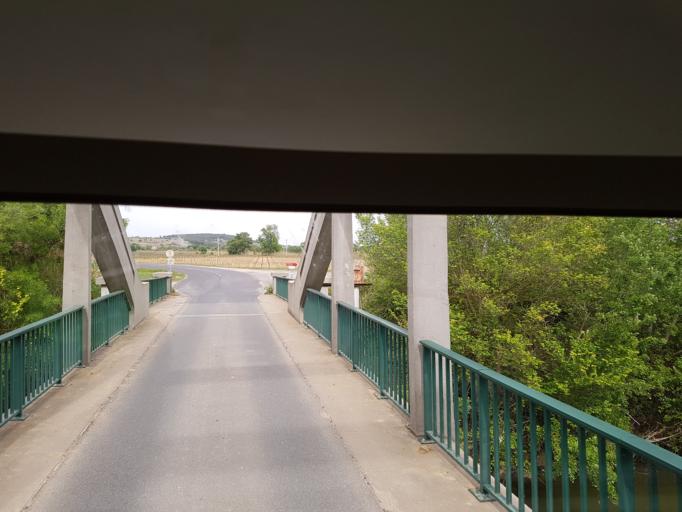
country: FR
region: Languedoc-Roussillon
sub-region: Departement de l'Aude
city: Fleury
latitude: 43.2444
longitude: 3.1527
